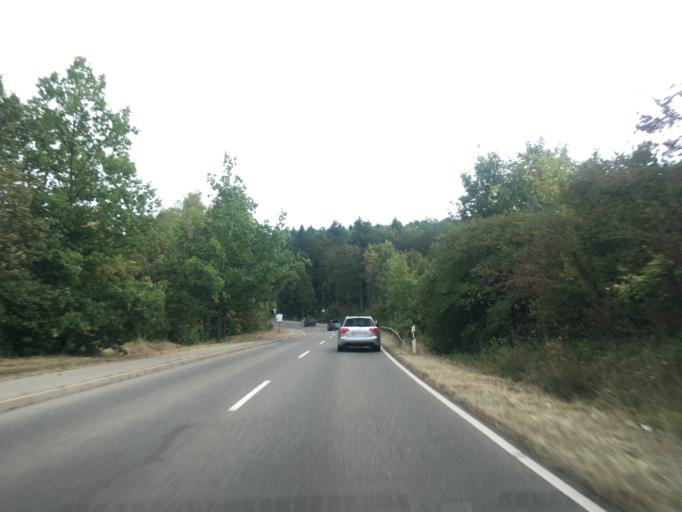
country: DE
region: Baden-Wuerttemberg
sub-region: Tuebingen Region
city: Wannweil
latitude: 48.4737
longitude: 9.1529
